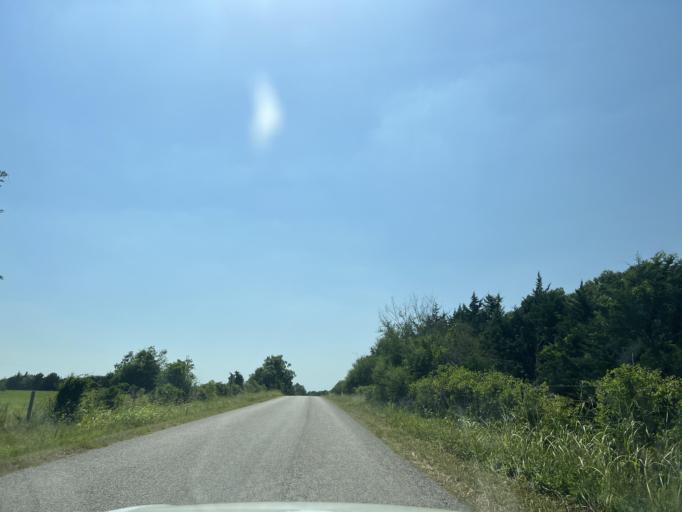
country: US
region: Texas
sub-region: Washington County
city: Brenham
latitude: 30.1534
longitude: -96.4796
